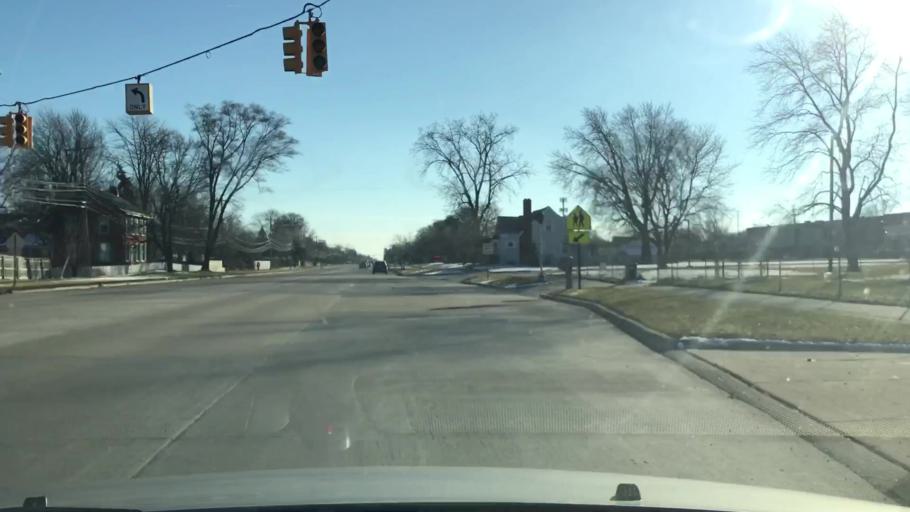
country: US
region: Michigan
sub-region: Oakland County
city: Troy
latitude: 42.5834
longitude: -83.1092
